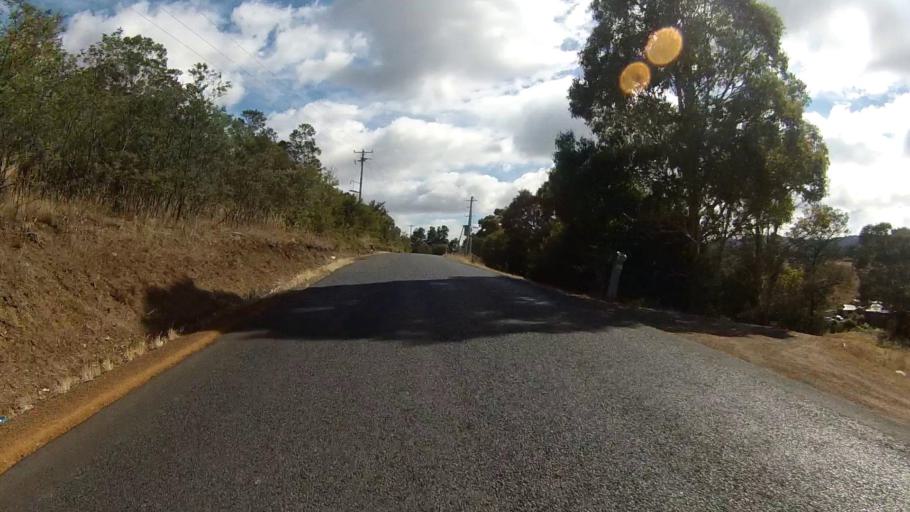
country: AU
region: Tasmania
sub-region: Brighton
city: Old Beach
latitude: -42.7742
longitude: 147.2875
